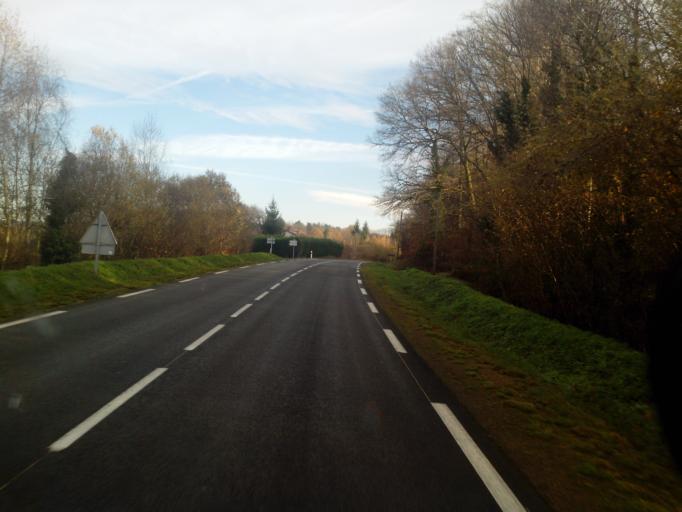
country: FR
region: Limousin
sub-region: Departement de la Haute-Vienne
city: Saint-Leonard-de-Noblat
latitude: 45.7773
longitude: 1.5090
